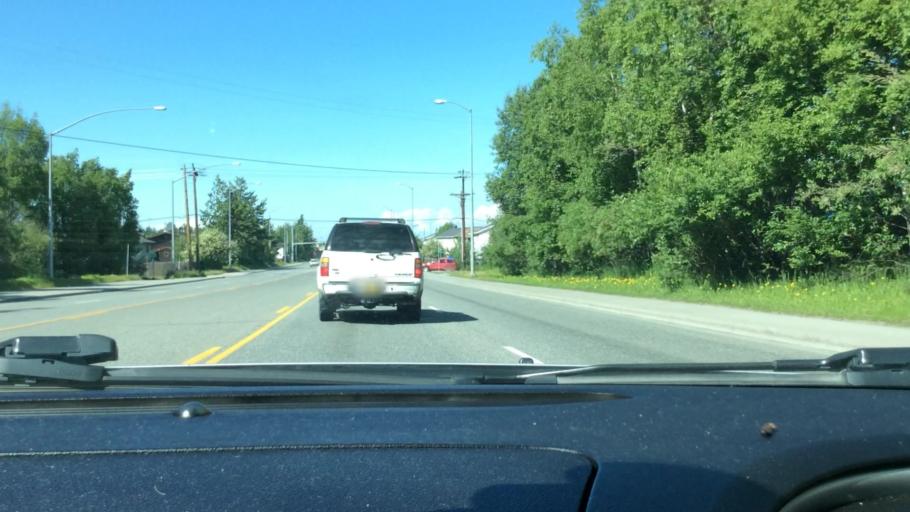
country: US
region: Alaska
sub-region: Anchorage Municipality
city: Anchorage
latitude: 61.2159
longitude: -149.7784
